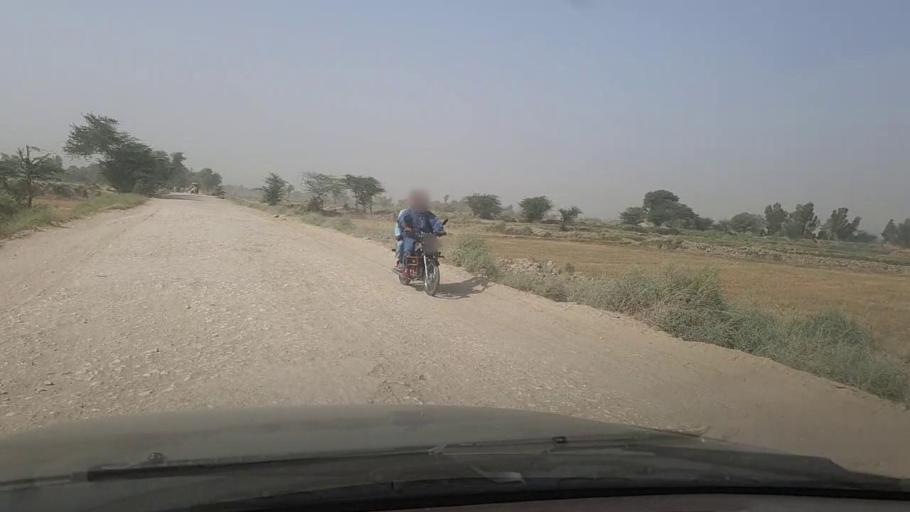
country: PK
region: Sindh
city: Shikarpur
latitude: 27.9279
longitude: 68.6158
